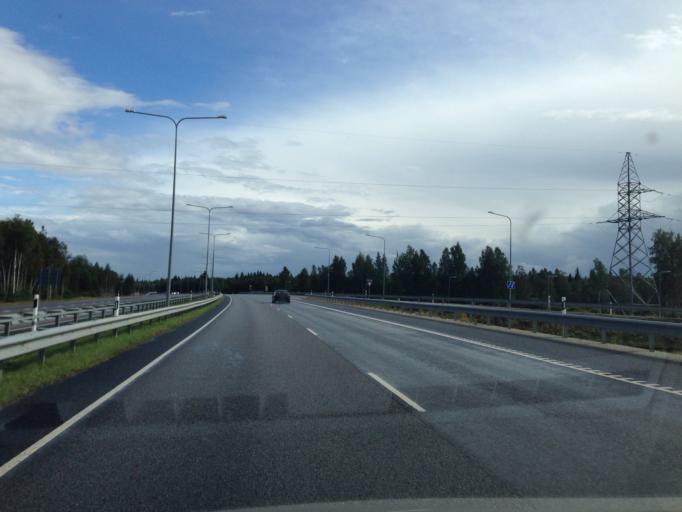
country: EE
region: Jaervamaa
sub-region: Paide linn
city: Paide
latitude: 58.9016
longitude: 25.6379
